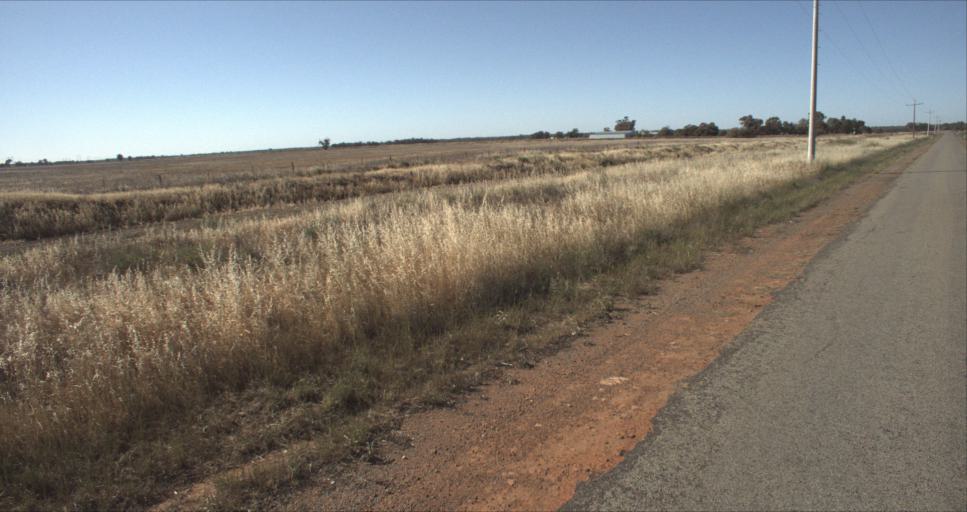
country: AU
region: New South Wales
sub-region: Leeton
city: Leeton
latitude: -34.5786
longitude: 146.3092
